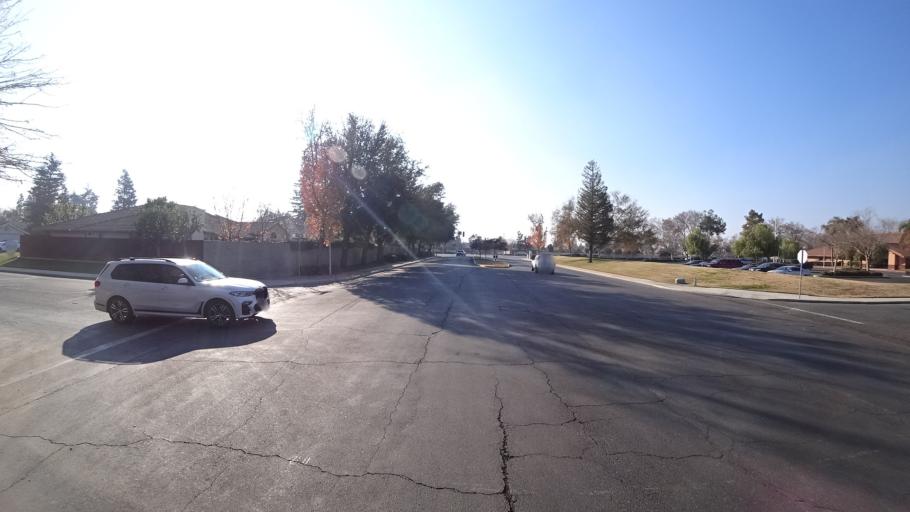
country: US
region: California
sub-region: Kern County
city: Greenacres
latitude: 35.3351
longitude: -119.1118
